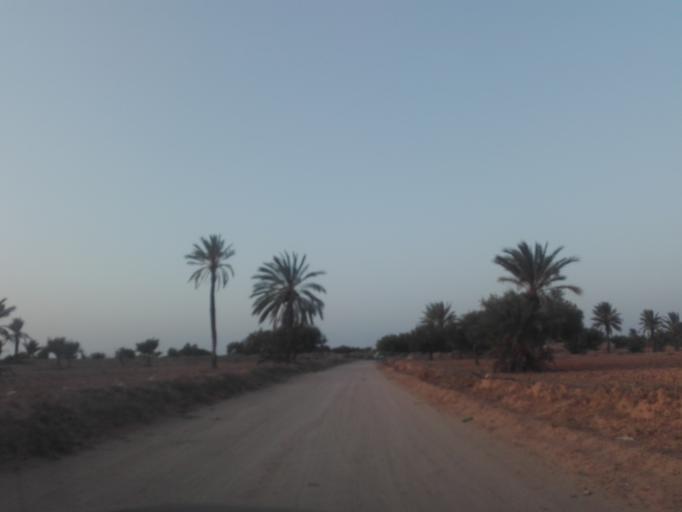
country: TN
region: Madanin
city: Houmt Souk
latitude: 33.7409
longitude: 10.7647
